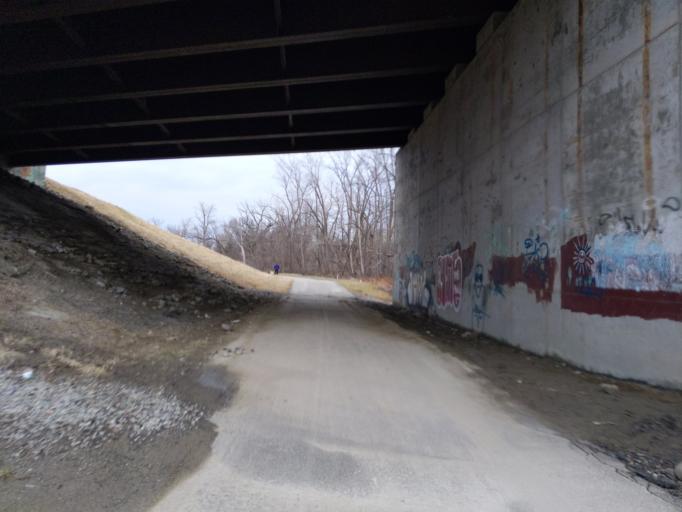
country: US
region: New York
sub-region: Chemung County
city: Elmira
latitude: 42.0956
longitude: -76.7880
